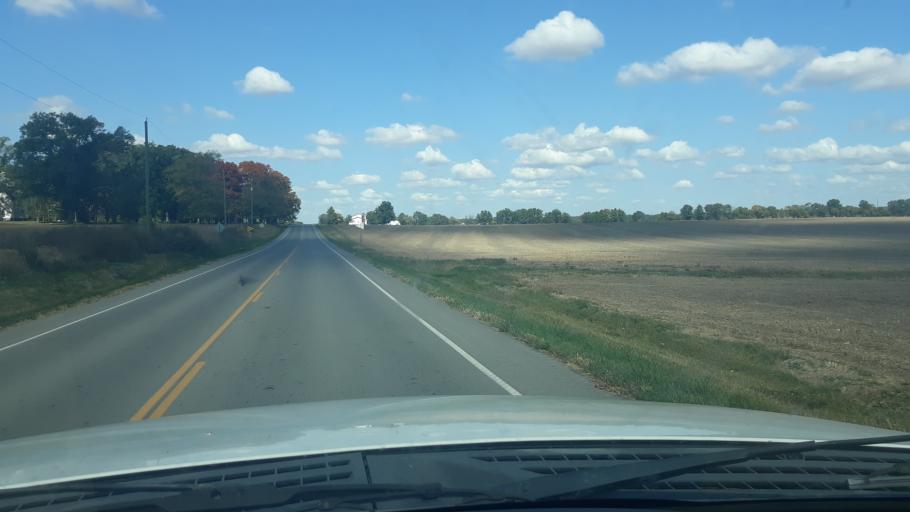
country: US
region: Illinois
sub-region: Saline County
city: Eldorado
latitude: 37.7907
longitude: -88.4848
